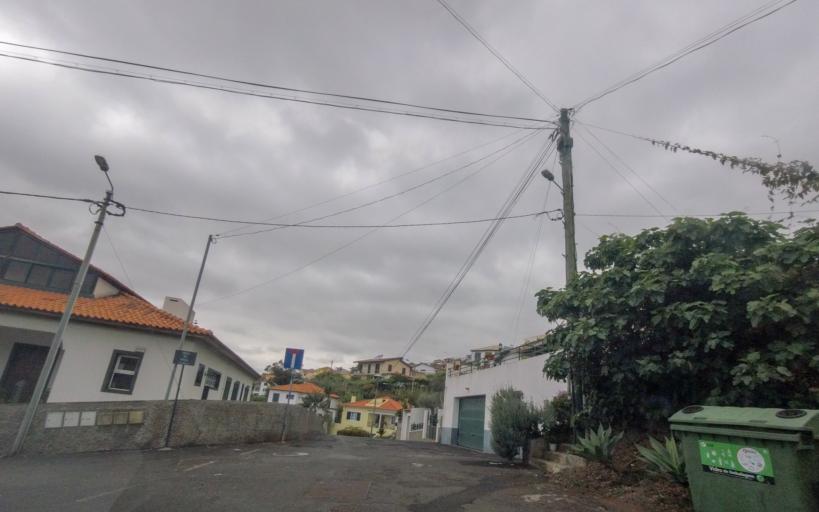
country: PT
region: Madeira
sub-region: Funchal
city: Nossa Senhora do Monte
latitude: 32.6595
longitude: -16.8825
